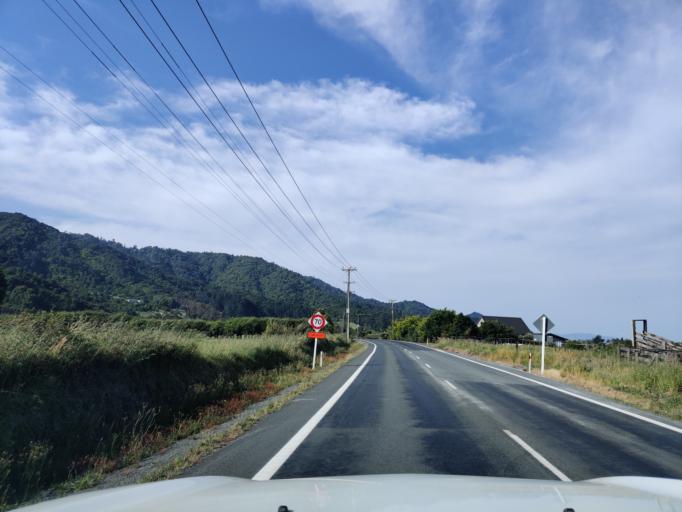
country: NZ
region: Waikato
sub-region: Waikato District
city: Ngaruawahia
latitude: -37.6407
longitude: 175.1486
